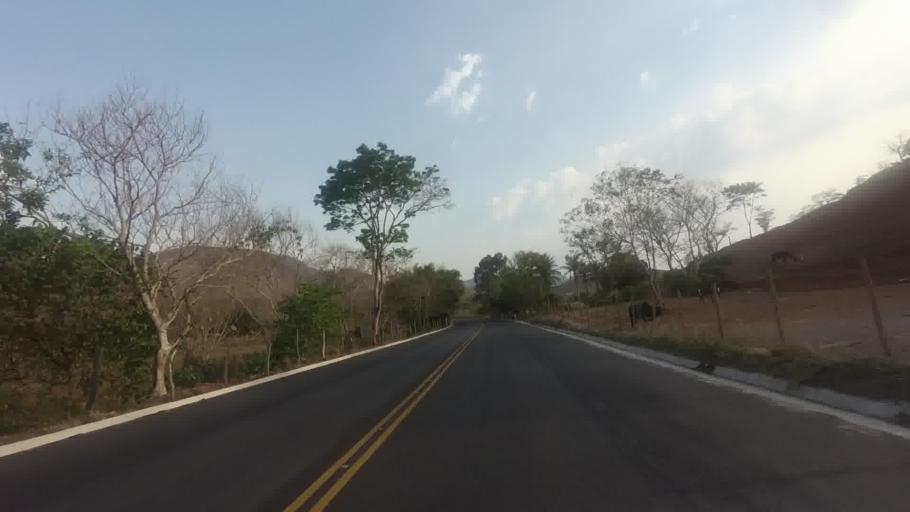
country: BR
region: Rio de Janeiro
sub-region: Cambuci
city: Cambuci
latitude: -21.4397
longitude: -42.0100
